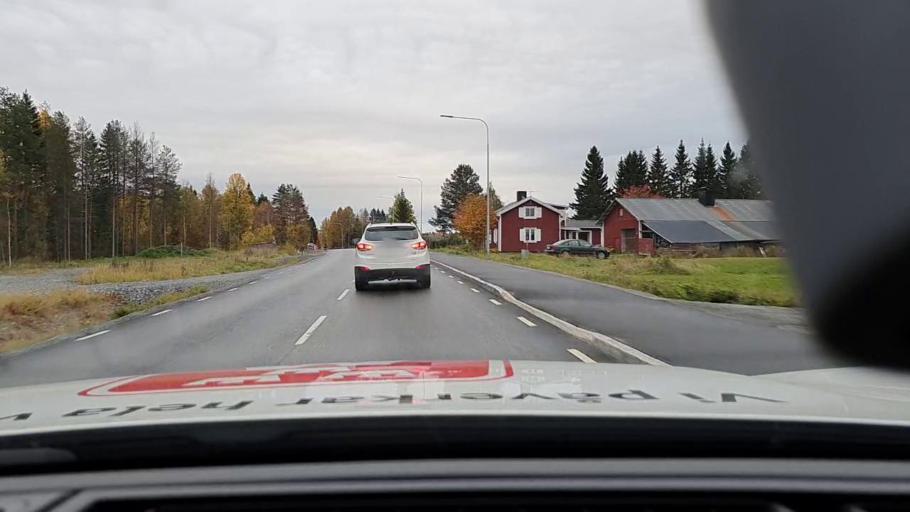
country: SE
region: Norrbotten
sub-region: Bodens Kommun
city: Saevast
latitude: 65.7747
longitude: 21.6954
